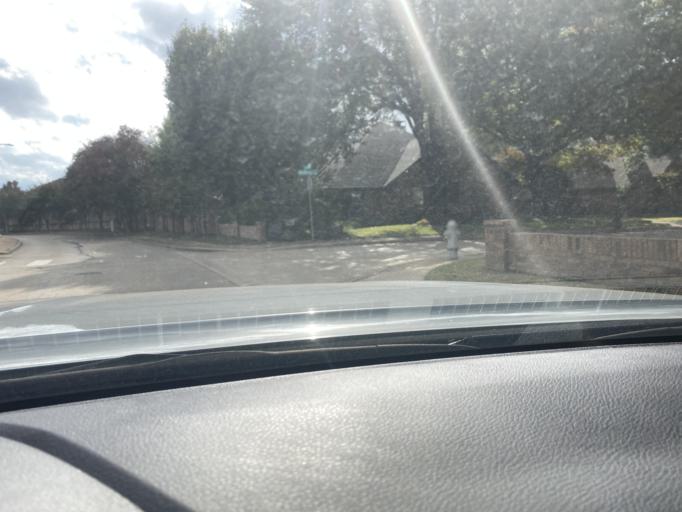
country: US
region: Texas
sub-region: Dallas County
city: Addison
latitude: 33.0010
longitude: -96.7856
